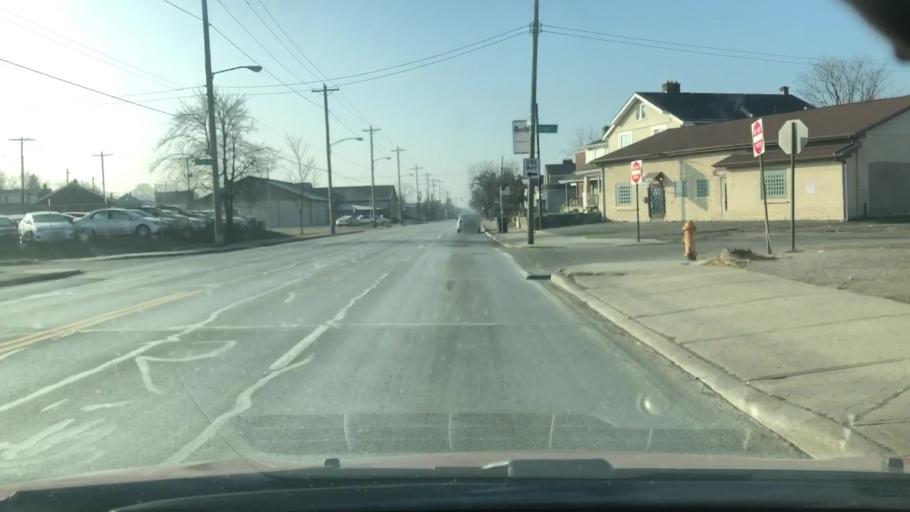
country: US
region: Ohio
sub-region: Franklin County
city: Bexley
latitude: 40.0049
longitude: -82.9728
